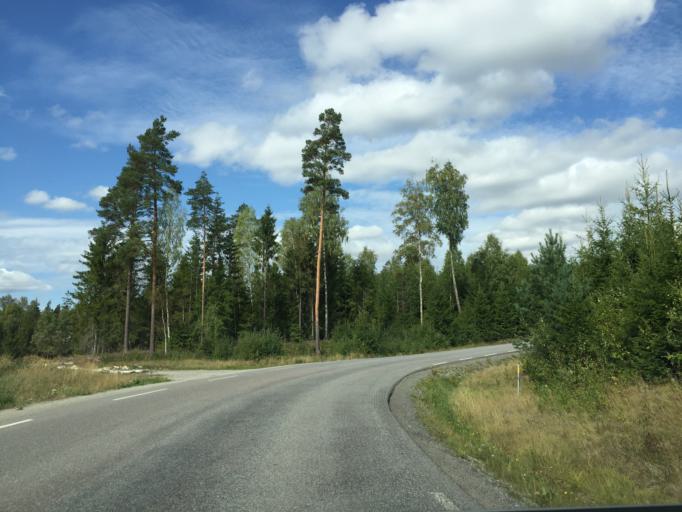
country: NO
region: Ostfold
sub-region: Hobol
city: Elvestad
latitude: 59.6058
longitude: 10.9029
